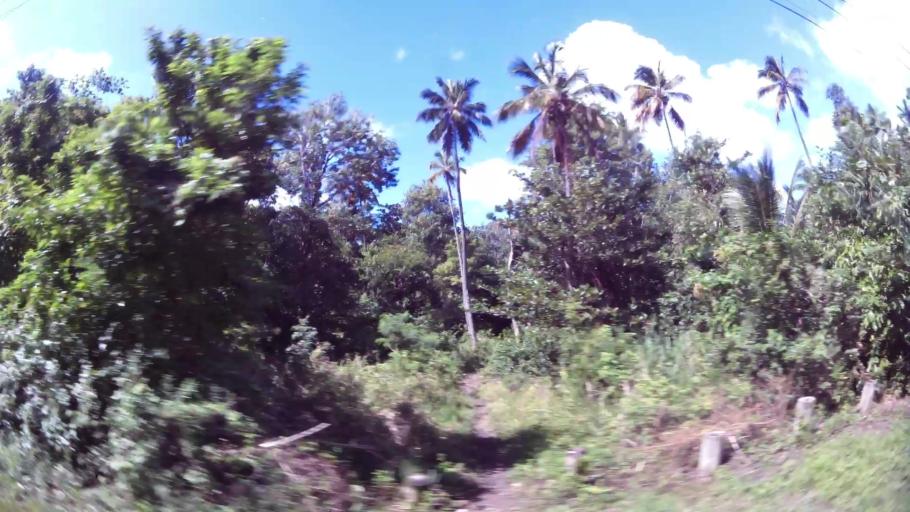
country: DM
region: Saint John
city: Portsmouth
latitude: 15.5928
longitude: -61.4634
